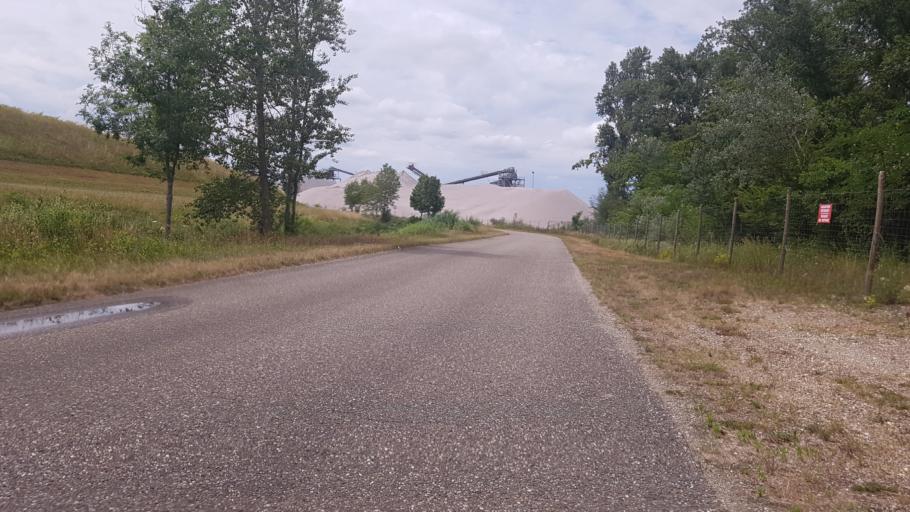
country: DE
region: Baden-Wuerttemberg
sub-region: Karlsruhe Region
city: Hugelsheim
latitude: 48.7961
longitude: 8.0728
